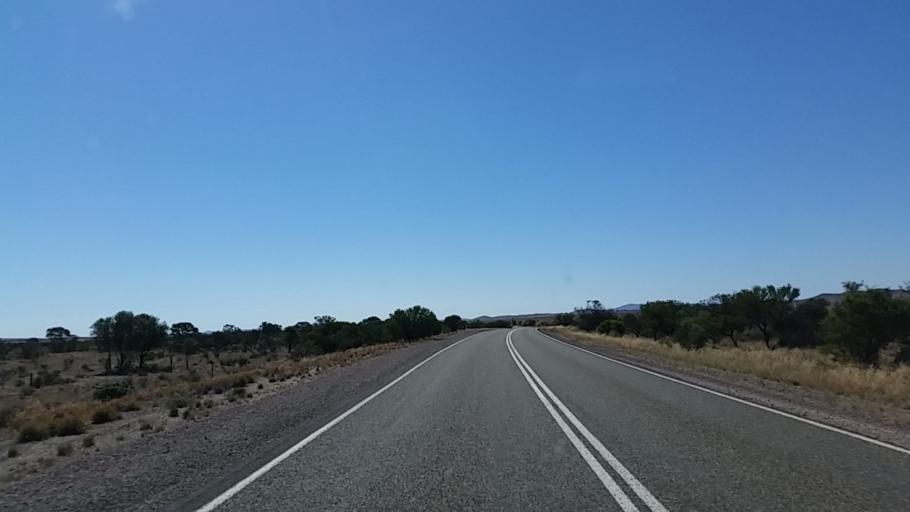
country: AU
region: South Australia
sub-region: Flinders Ranges
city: Quorn
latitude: -32.4621
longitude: 138.5378
